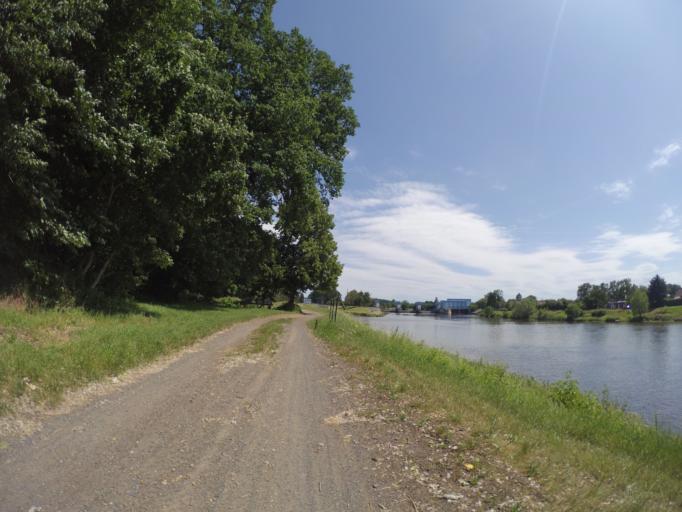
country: CZ
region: Central Bohemia
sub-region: Okres Nymburk
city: Sadska
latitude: 50.1717
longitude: 14.9367
